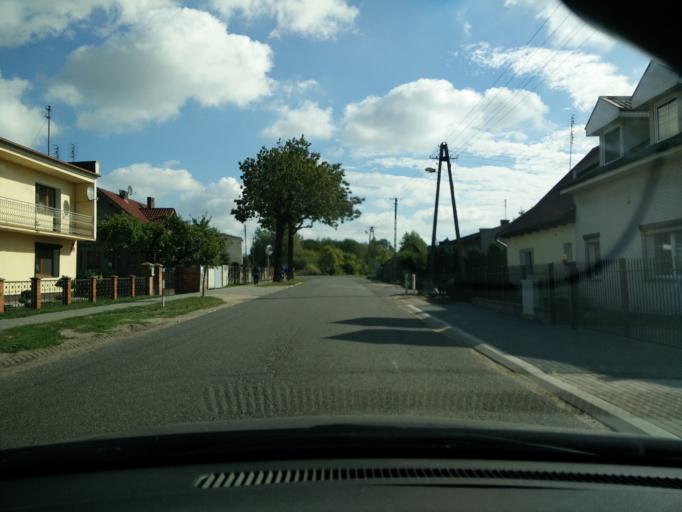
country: PL
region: Greater Poland Voivodeship
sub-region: Powiat sredzki
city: Dominowo
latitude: 52.3202
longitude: 17.3726
